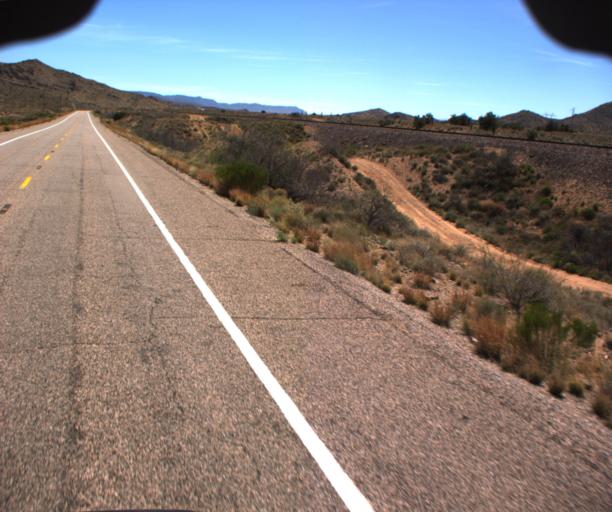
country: US
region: Arizona
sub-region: Mohave County
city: New Kingman-Butler
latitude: 35.3904
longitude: -113.7419
